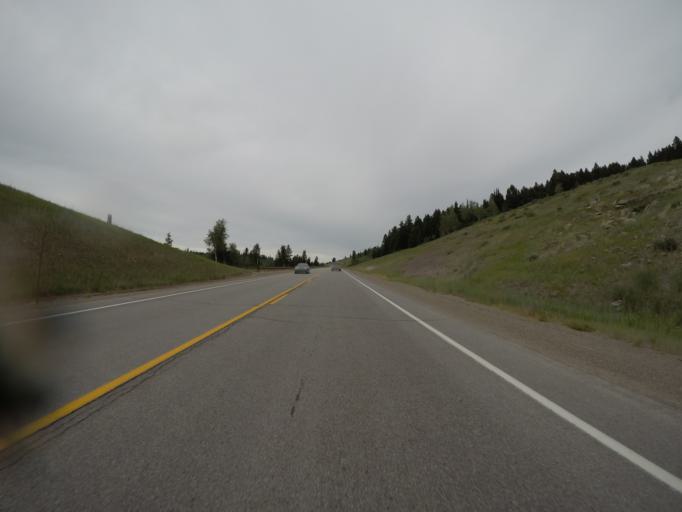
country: US
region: Wyoming
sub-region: Lincoln County
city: Afton
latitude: 42.4948
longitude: -110.9110
